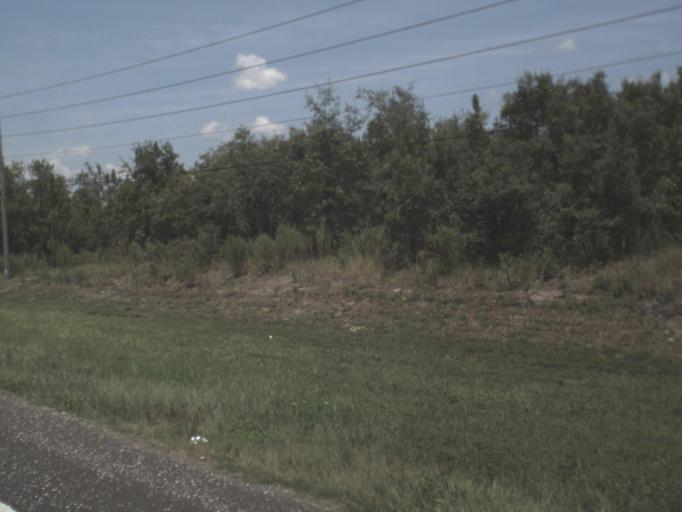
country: US
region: Florida
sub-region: Hernando County
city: Timber Pines
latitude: 28.4852
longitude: -82.6048
